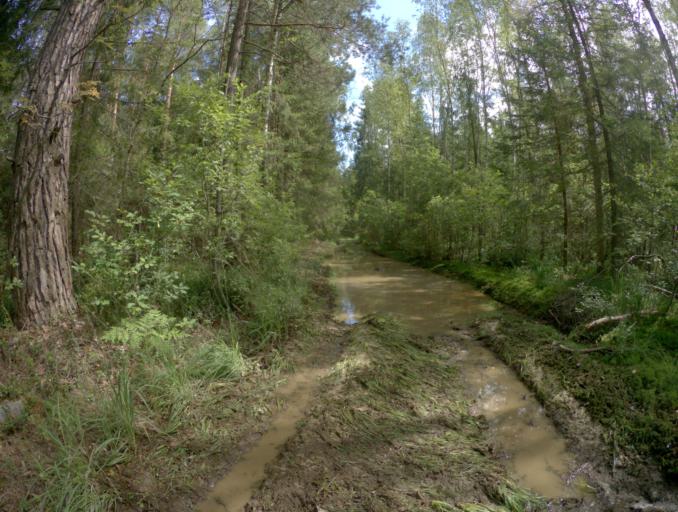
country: RU
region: Vladimir
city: Orgtrud
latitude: 56.0761
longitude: 40.6158
